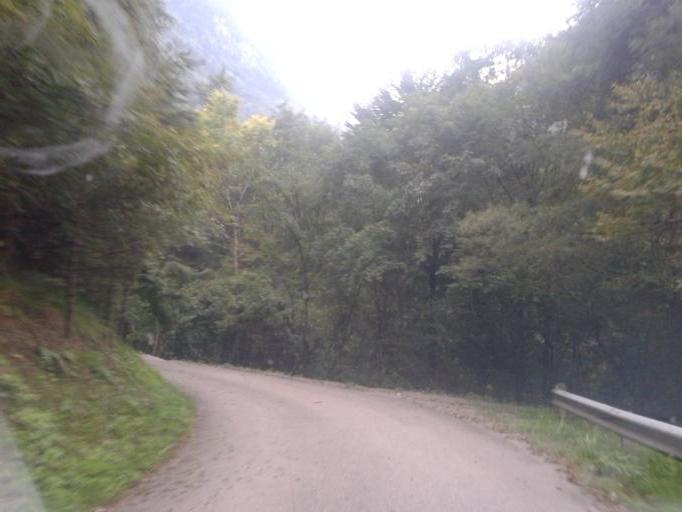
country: IT
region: Trentino-Alto Adige
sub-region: Provincia di Trento
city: Storo
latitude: 45.8412
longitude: 10.6143
